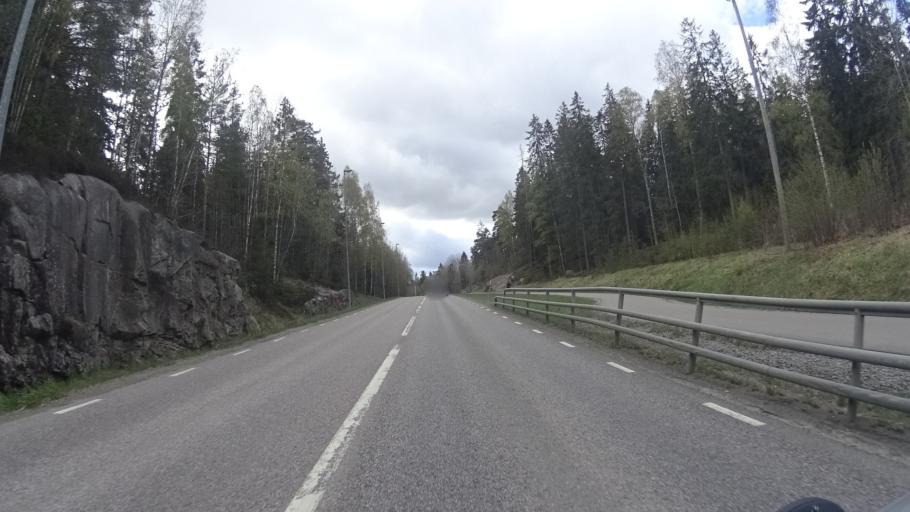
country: SE
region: Stockholm
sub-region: Botkyrka Kommun
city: Tullinge
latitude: 59.2050
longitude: 17.9246
